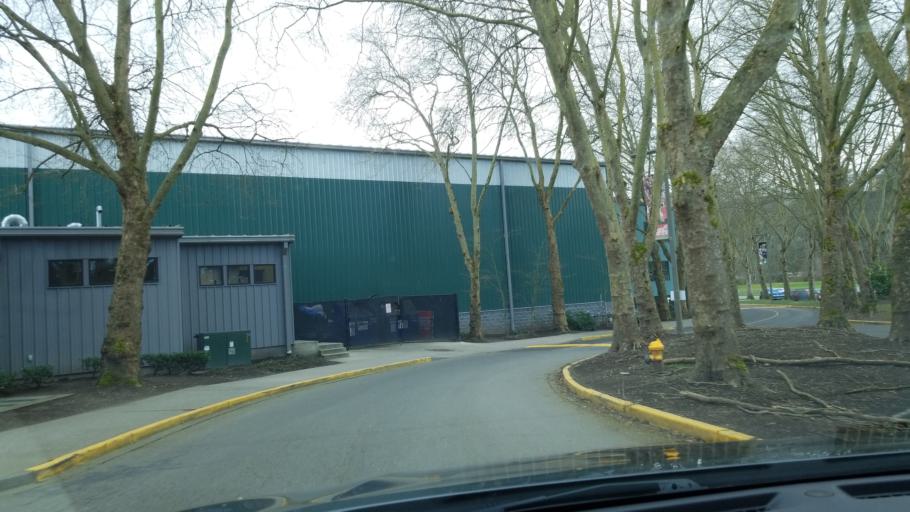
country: US
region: Washington
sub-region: King County
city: Tukwila
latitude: 47.4706
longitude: -122.2498
